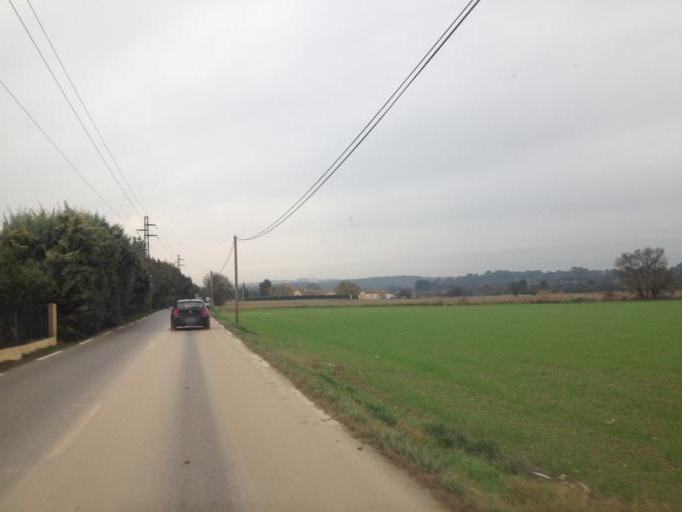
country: FR
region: Provence-Alpes-Cote d'Azur
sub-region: Departement des Bouches-du-Rhone
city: Eguilles
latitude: 43.5177
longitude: 5.3515
